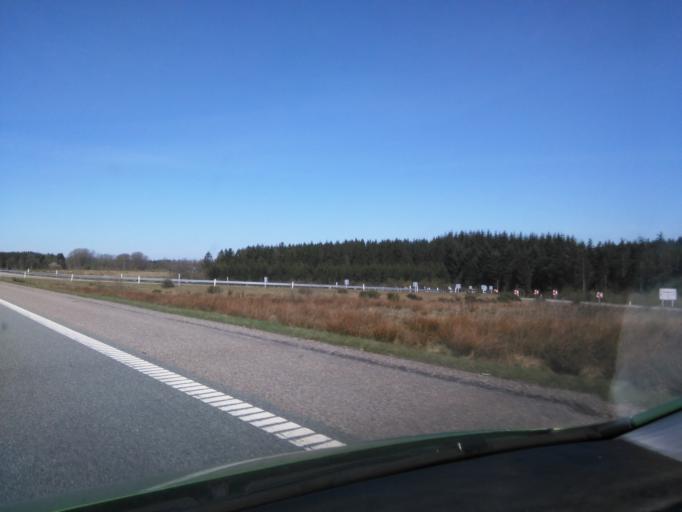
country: DK
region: South Denmark
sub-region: Vejle Kommune
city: Give
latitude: 55.8351
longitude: 9.3099
